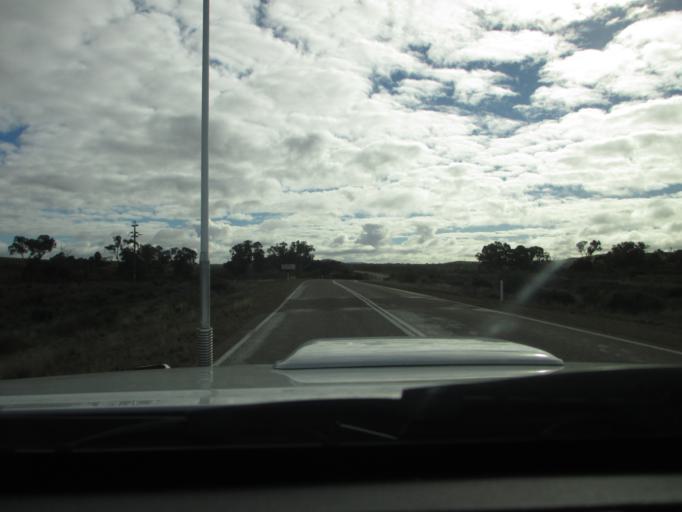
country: AU
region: South Australia
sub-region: Flinders Ranges
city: Quorn
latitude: -32.3119
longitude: 138.4852
